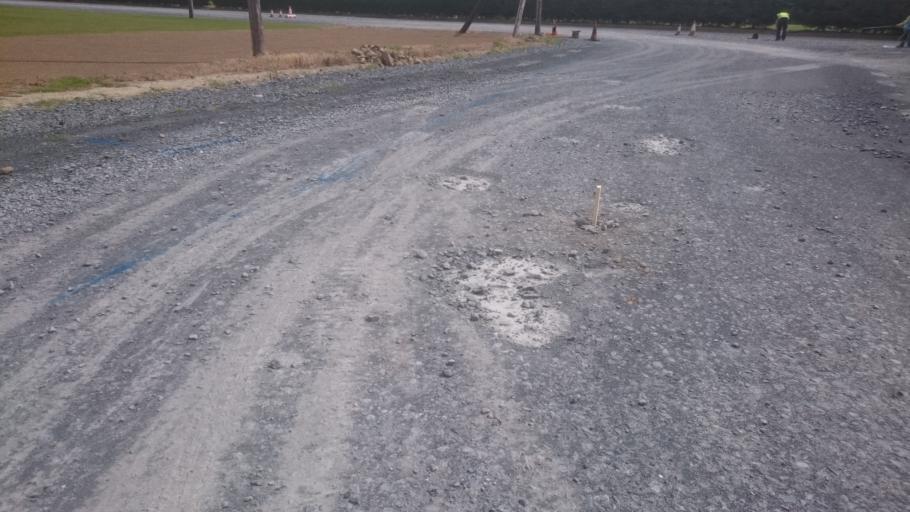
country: IE
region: Leinster
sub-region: Kilkenny
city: Kilkenny
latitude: 52.5966
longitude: -7.2613
